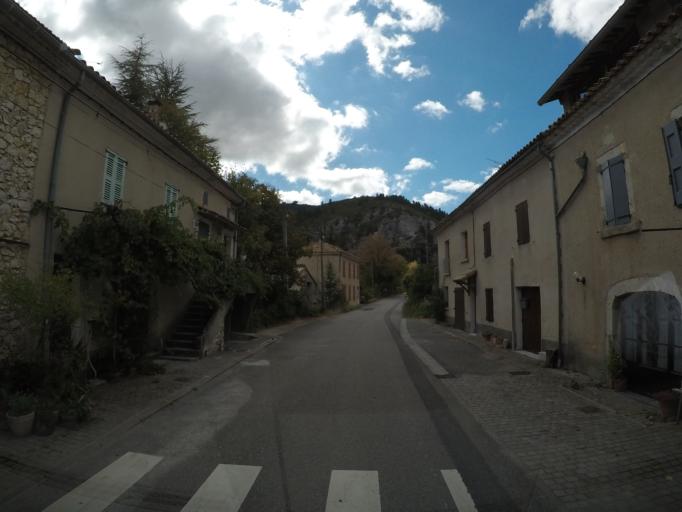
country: FR
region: Provence-Alpes-Cote d'Azur
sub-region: Departement des Hautes-Alpes
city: Laragne-Monteglin
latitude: 44.1744
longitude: 5.6382
